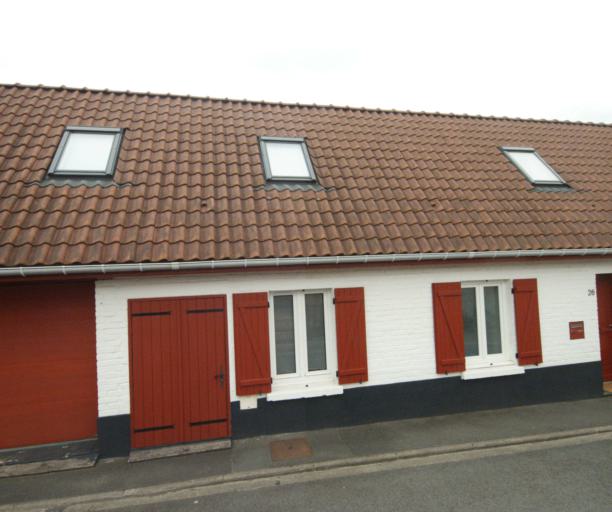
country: FR
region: Nord-Pas-de-Calais
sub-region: Departement du Nord
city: Fretin
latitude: 50.5543
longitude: 3.1356
